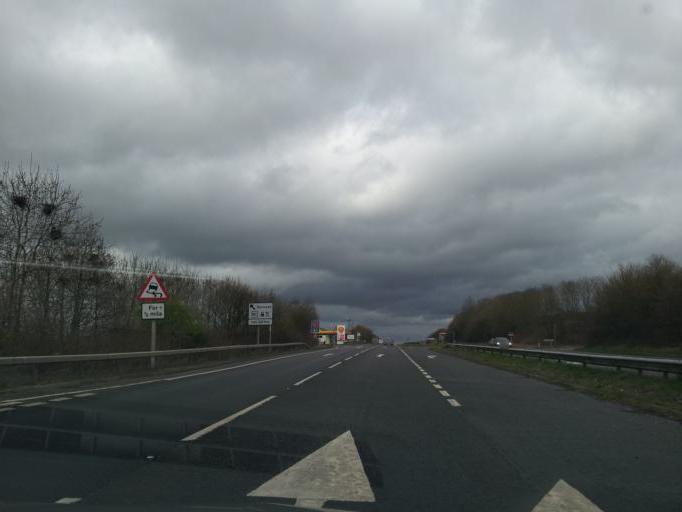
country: GB
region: England
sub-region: Somerset
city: Stoke-sub-Hamdon
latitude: 50.9809
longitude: -2.7185
